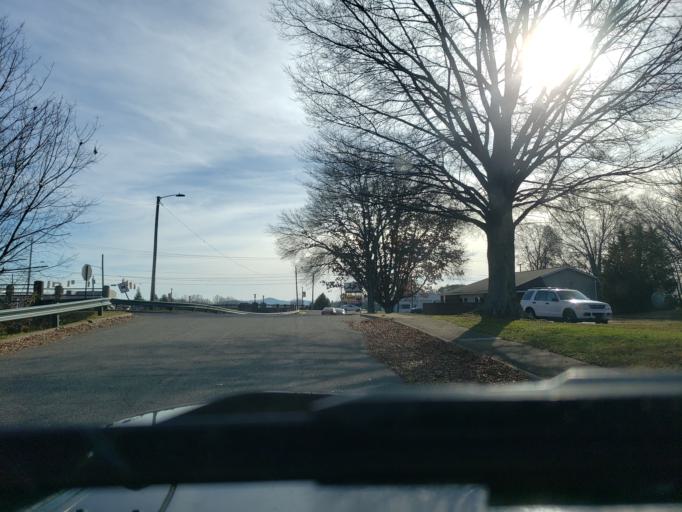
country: US
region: North Carolina
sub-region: Cleveland County
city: Kings Mountain
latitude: 35.2420
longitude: -81.3447
